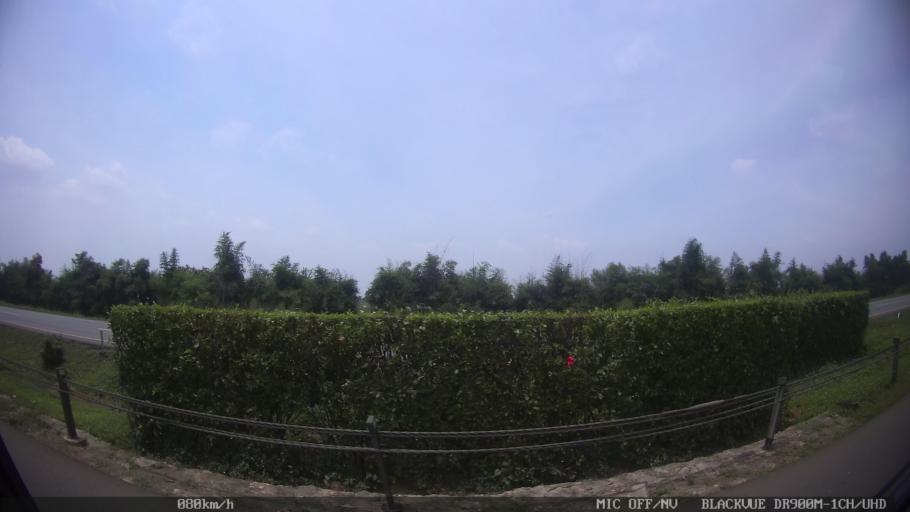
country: ID
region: West Java
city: Kresek
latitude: -6.1574
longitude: 106.3253
